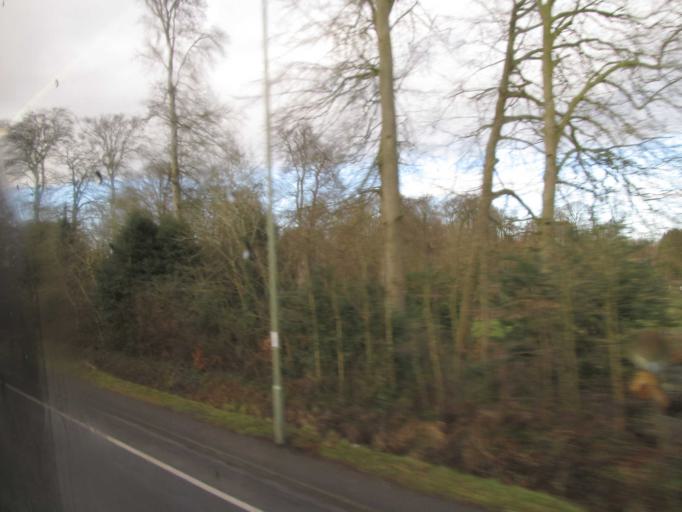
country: GB
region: England
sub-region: Hampshire
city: Basingstoke
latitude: 51.2455
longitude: -1.1257
